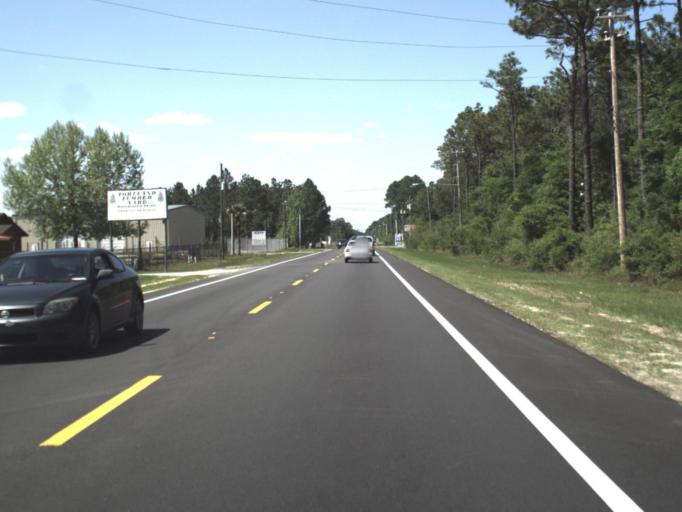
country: US
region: Florida
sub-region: Bay County
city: Hiland Park
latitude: 30.1873
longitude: -85.6078
